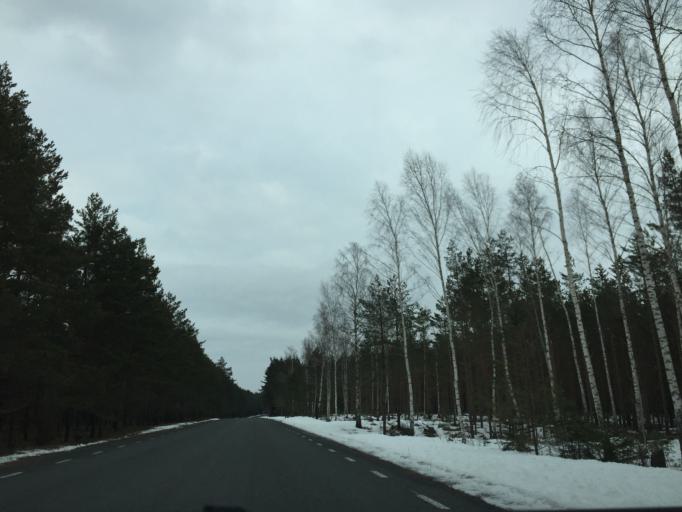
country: EE
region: Saare
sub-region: Kuressaare linn
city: Kuressaare
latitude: 58.4236
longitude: 22.1769
